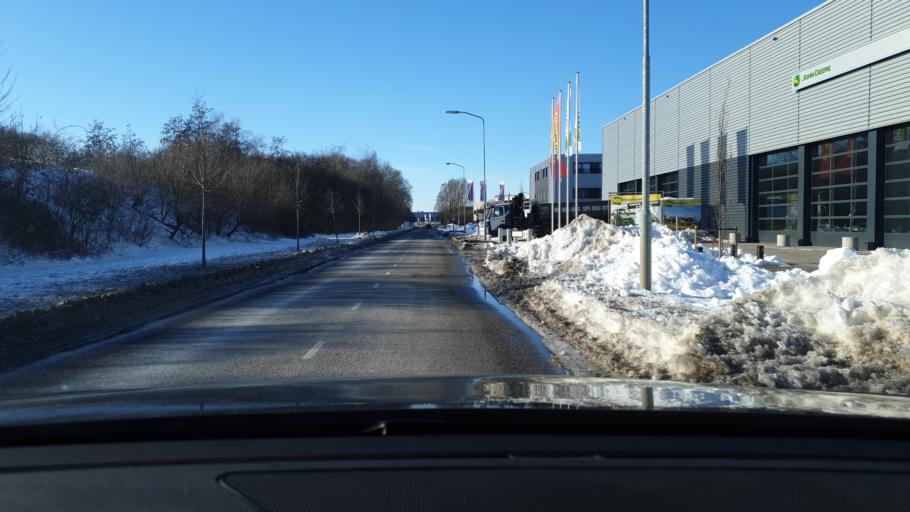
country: NL
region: Gelderland
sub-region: Gemeente Nijmegen
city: Lindenholt
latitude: 51.8211
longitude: 5.7644
